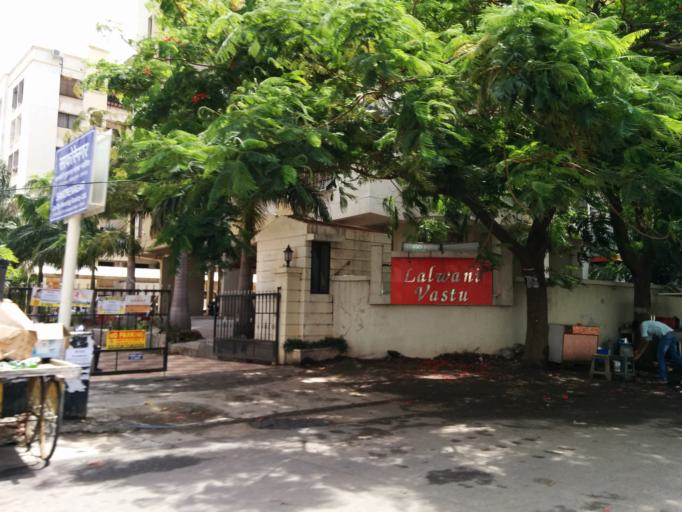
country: IN
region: Maharashtra
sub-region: Pune Division
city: Lohogaon
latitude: 18.5622
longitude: 73.9082
